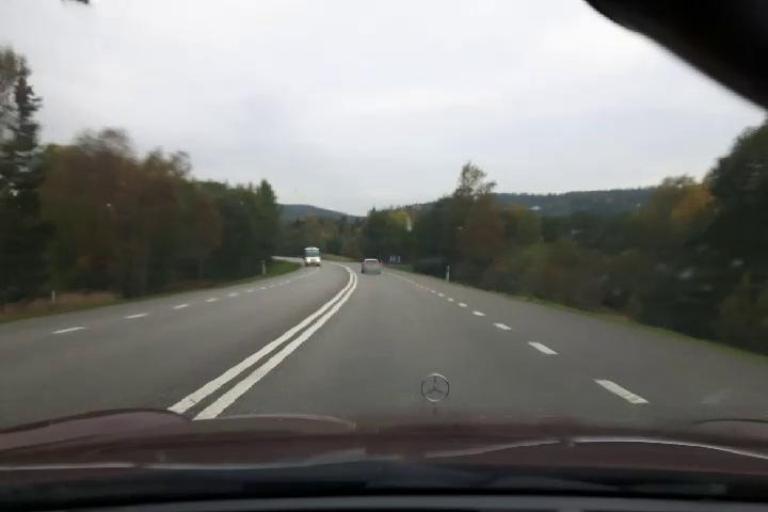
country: SE
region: Vaesternorrland
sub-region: Kramfors Kommun
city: Nordingra
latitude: 63.0238
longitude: 18.2975
